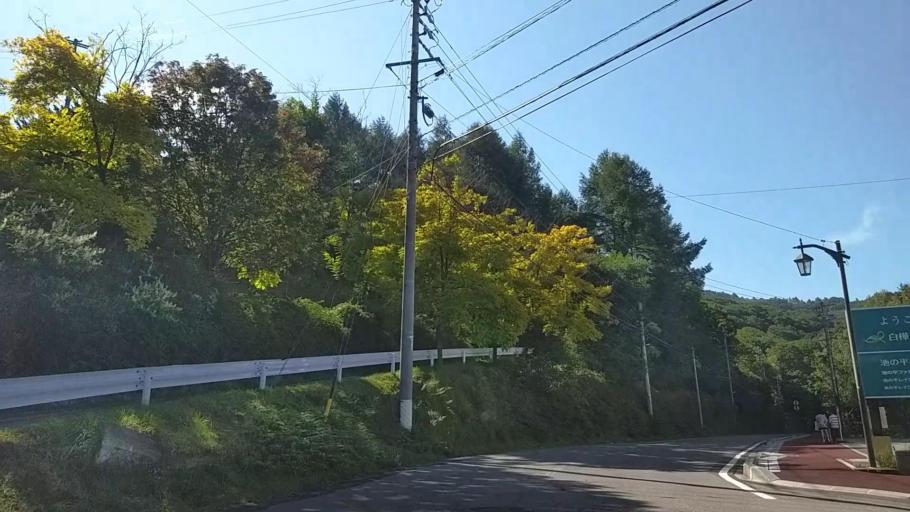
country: JP
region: Nagano
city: Chino
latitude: 36.1089
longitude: 138.2426
